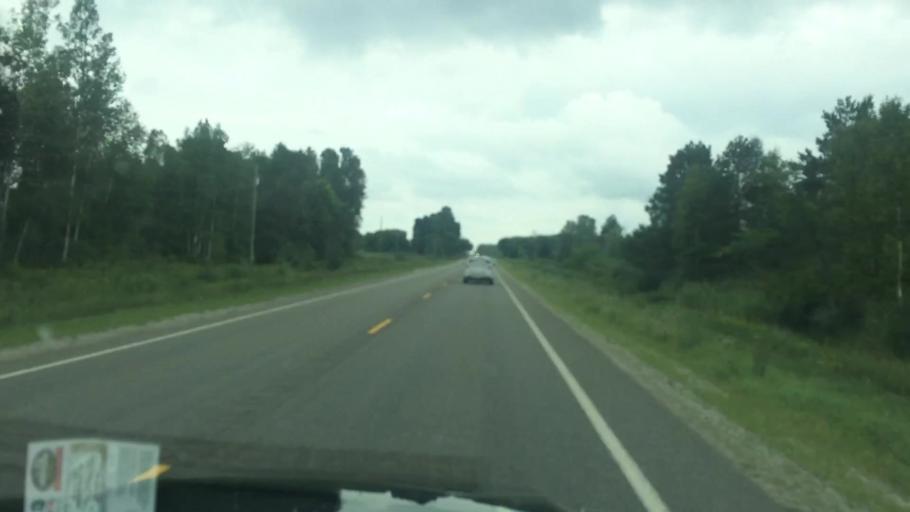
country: US
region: Michigan
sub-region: Tuscola County
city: Cass City
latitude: 43.6283
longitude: -83.0971
